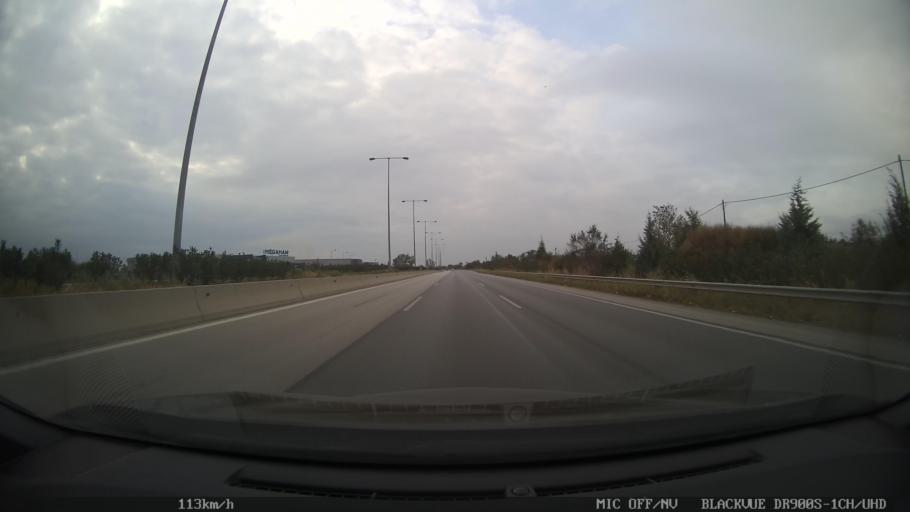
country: GR
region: Central Macedonia
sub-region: Nomos Thessalonikis
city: Nea Magnisia
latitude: 40.6790
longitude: 22.8323
